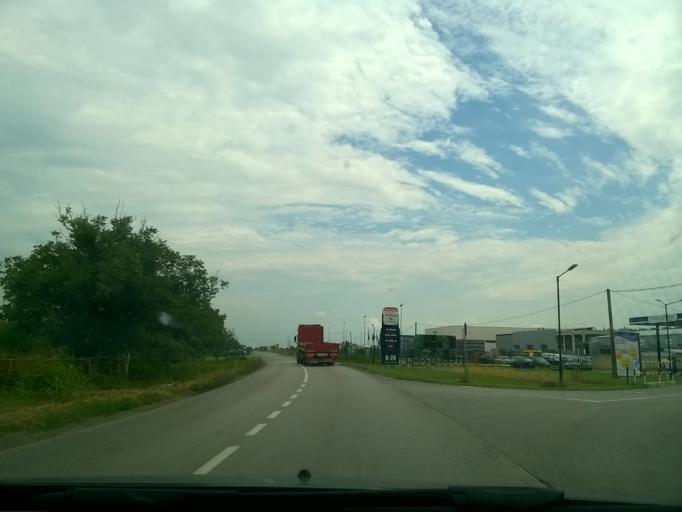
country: RS
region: Autonomna Pokrajina Vojvodina
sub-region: Srednjebanatski Okrug
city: Zrenjanin
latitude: 45.3826
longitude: 20.4325
